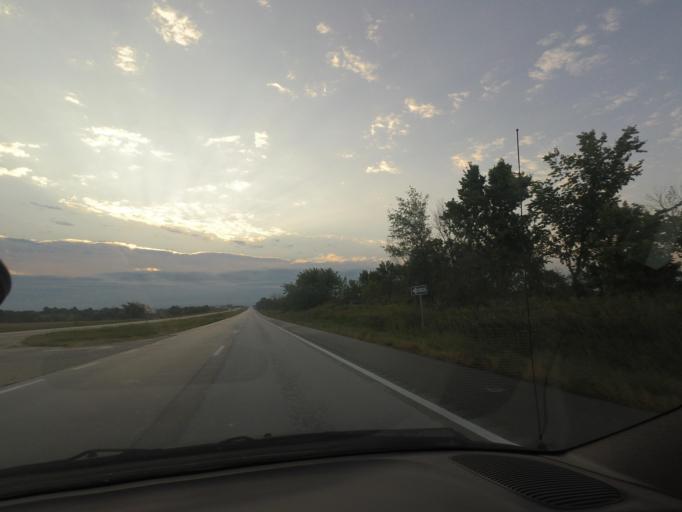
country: US
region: Missouri
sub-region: Shelby County
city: Shelbina
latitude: 39.7393
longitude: -92.2359
